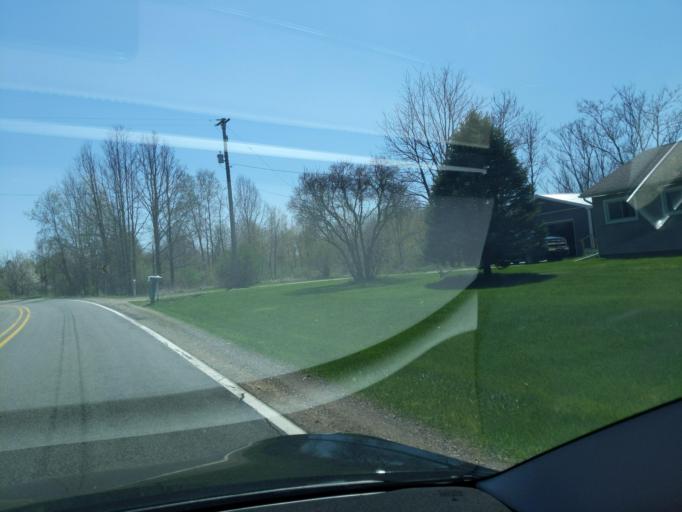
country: US
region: Michigan
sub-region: Ingham County
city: Stockbridge
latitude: 42.5273
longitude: -84.2783
